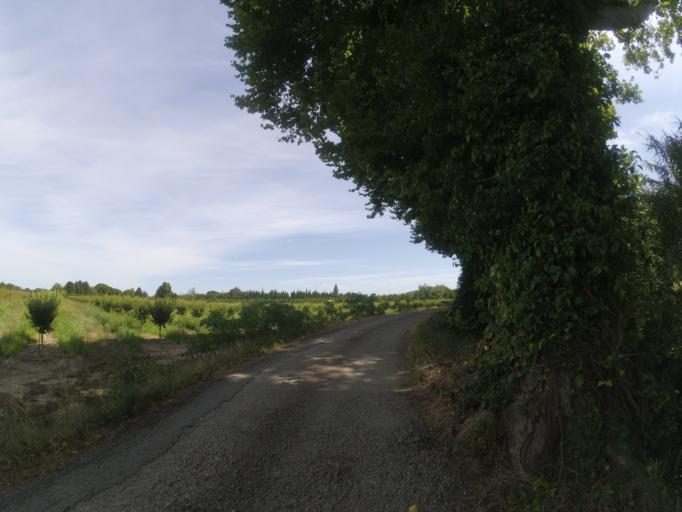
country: FR
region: Languedoc-Roussillon
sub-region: Departement des Pyrenees-Orientales
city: Ille-sur-Tet
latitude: 42.6764
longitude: 2.6503
